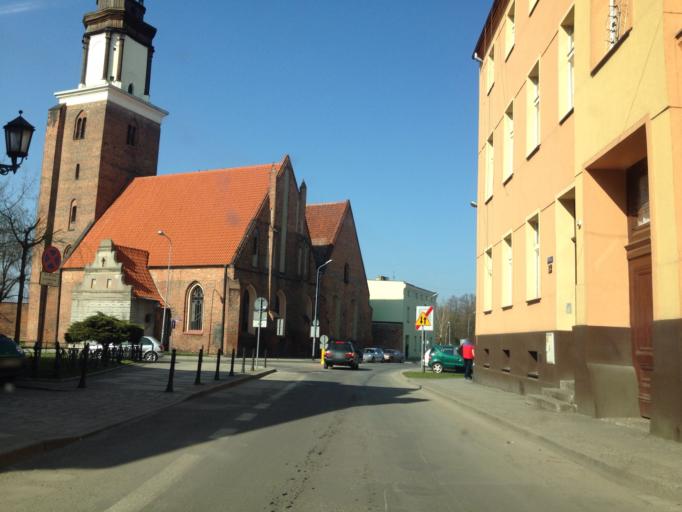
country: PL
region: Lower Silesian Voivodeship
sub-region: Powiat olesnicki
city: Olesnica
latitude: 51.2113
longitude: 17.3813
